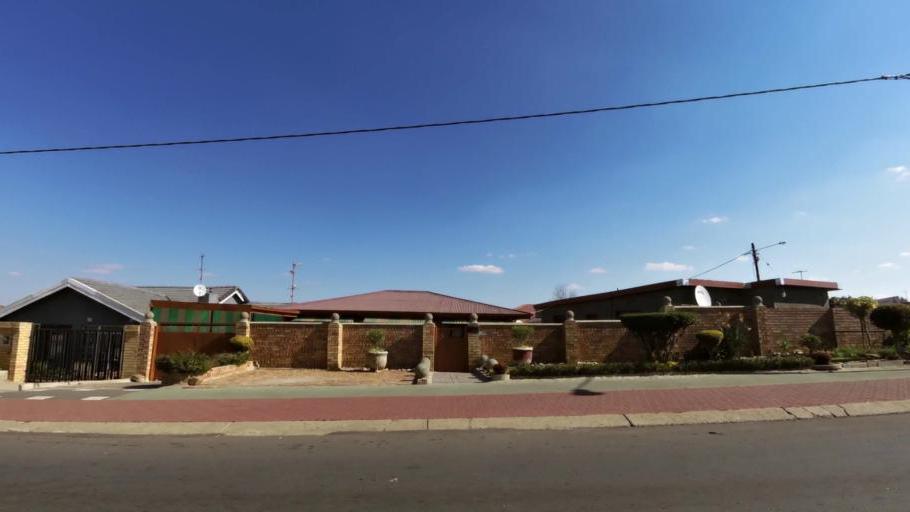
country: ZA
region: Gauteng
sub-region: City of Johannesburg Metropolitan Municipality
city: Soweto
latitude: -26.2432
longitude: 27.8944
